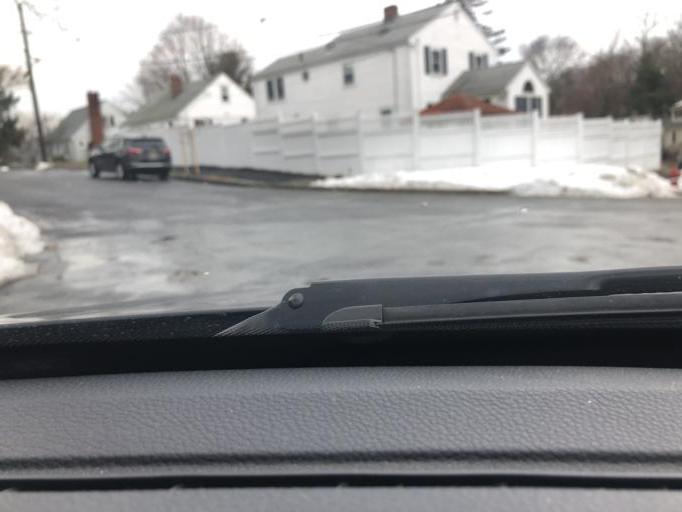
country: US
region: Massachusetts
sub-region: Middlesex County
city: Arlington
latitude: 42.4225
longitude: -71.1582
